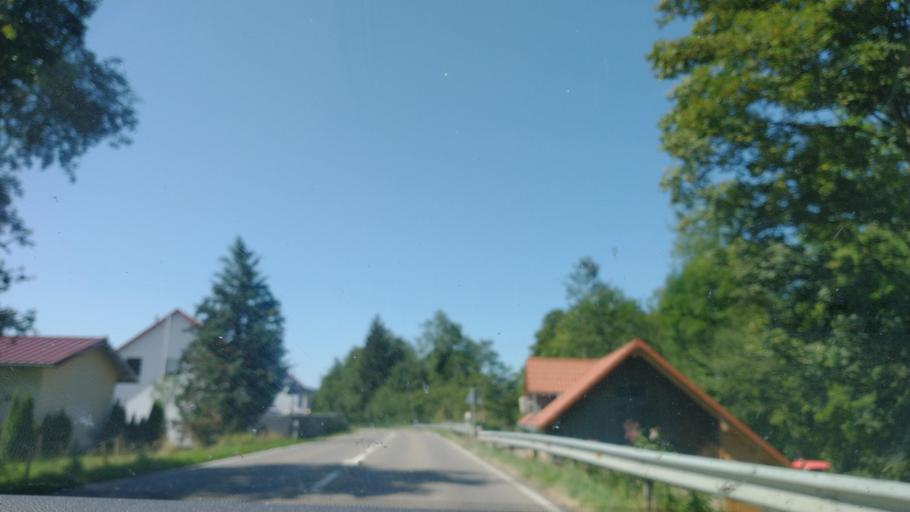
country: DE
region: Bavaria
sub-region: Swabia
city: Hergensweiler
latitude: 47.6468
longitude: 9.7678
